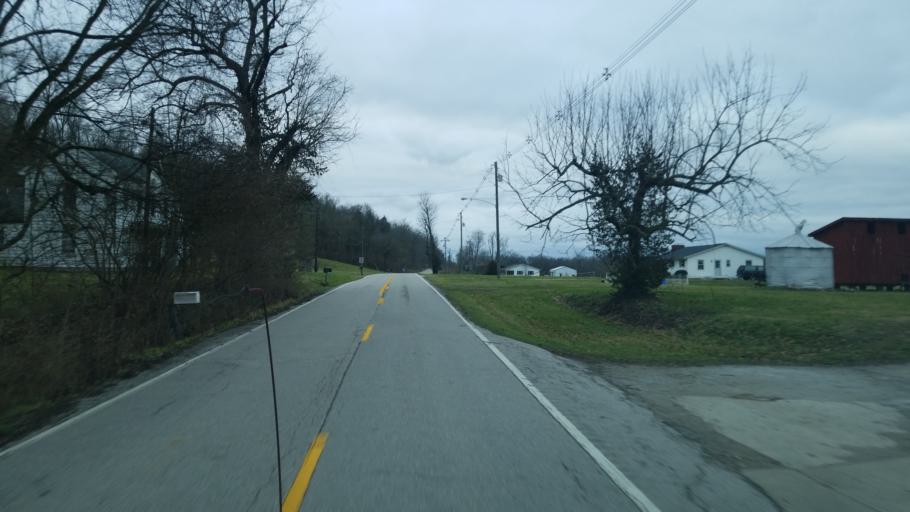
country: US
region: Ohio
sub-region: Clermont County
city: New Richmond
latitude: 38.8927
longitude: -84.2508
